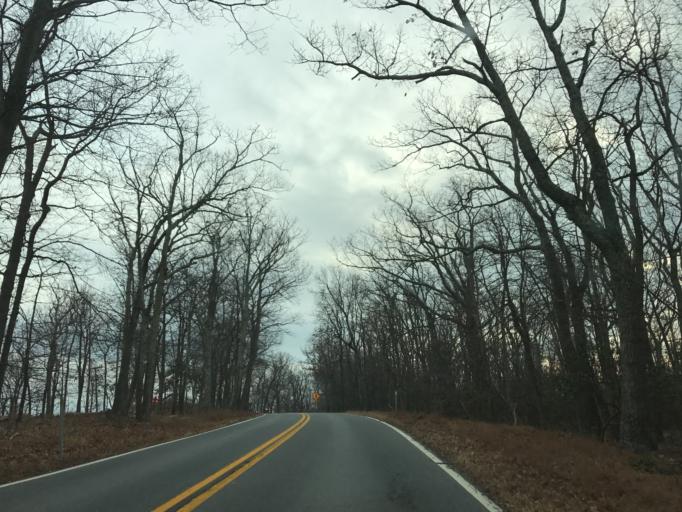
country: US
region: Maryland
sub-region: Frederick County
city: Braddock Heights
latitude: 39.4710
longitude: -77.4943
